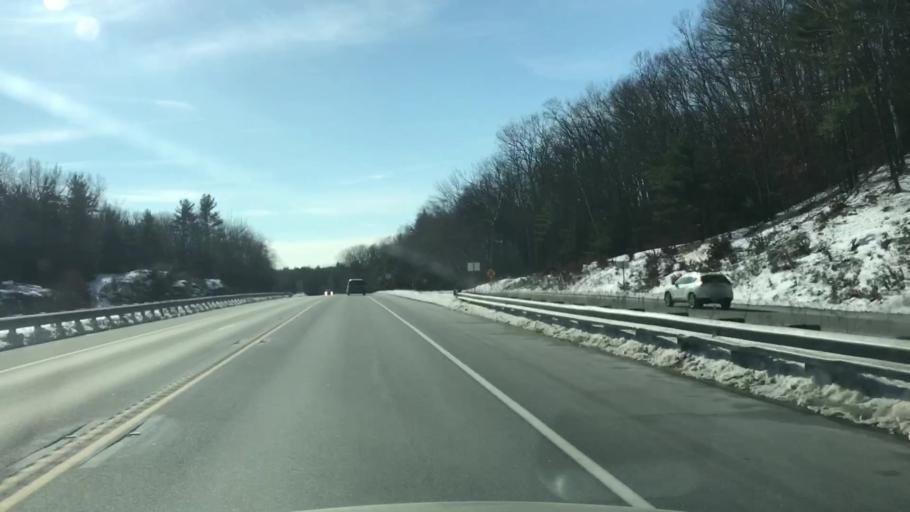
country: US
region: New Hampshire
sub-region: Hillsborough County
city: Milford
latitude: 42.8434
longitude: -71.6169
